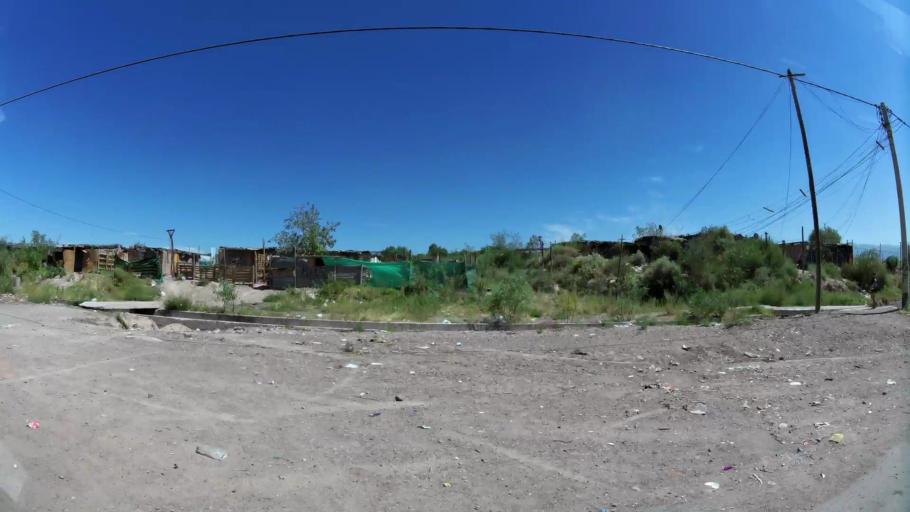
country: AR
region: Mendoza
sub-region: Departamento de Godoy Cruz
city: Godoy Cruz
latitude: -32.9462
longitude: -68.8764
